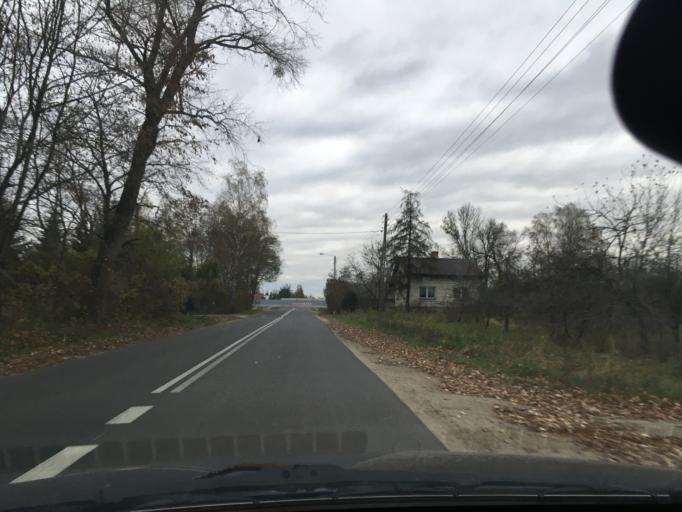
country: PL
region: Lodz Voivodeship
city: Zabia Wola
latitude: 52.0336
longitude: 20.6920
